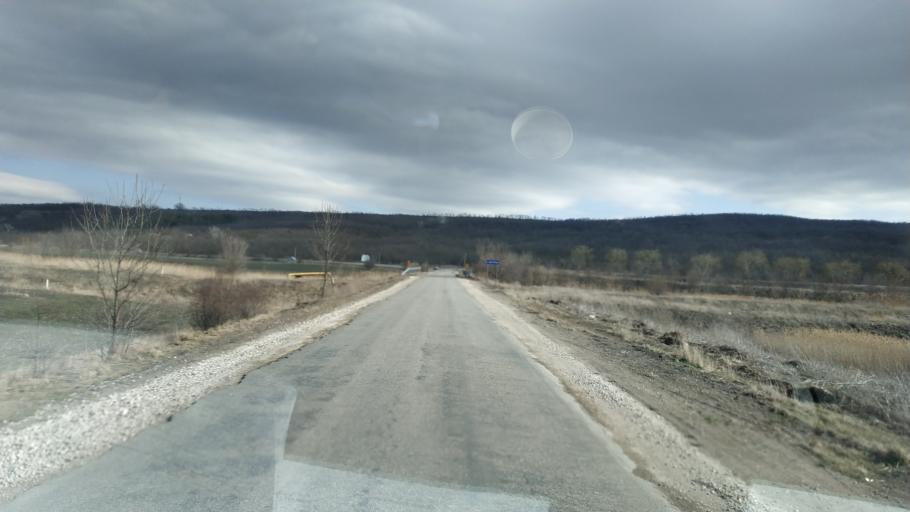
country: MD
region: Causeni
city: Causeni
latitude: 46.6373
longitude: 29.3725
